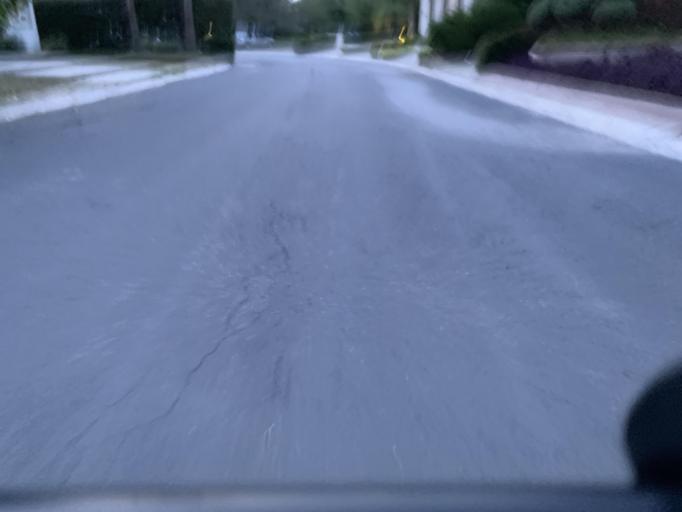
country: MX
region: Nuevo Leon
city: Santiago
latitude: 25.5065
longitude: -100.1862
